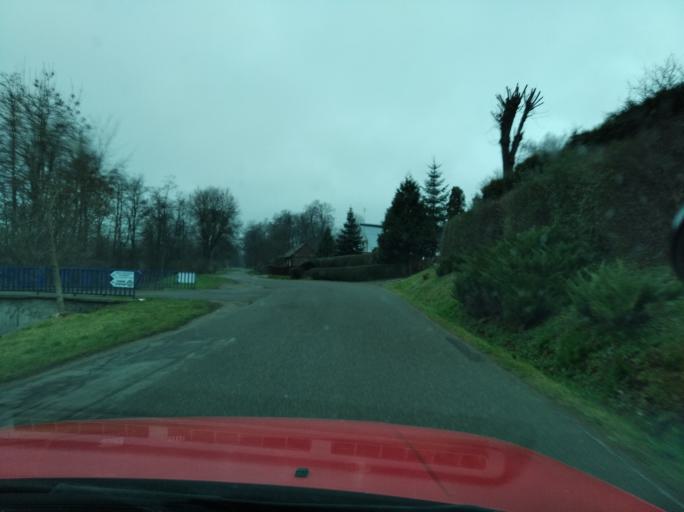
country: PL
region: Subcarpathian Voivodeship
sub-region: Powiat przeworski
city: Rozborz
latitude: 50.0532
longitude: 22.5469
